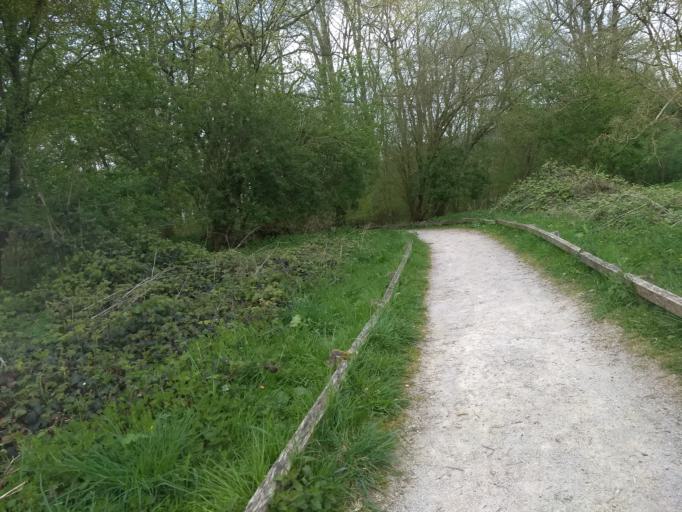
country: FR
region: Nord-Pas-de-Calais
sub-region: Departement du Pas-de-Calais
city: Maroeuil
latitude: 50.3375
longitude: 2.6999
